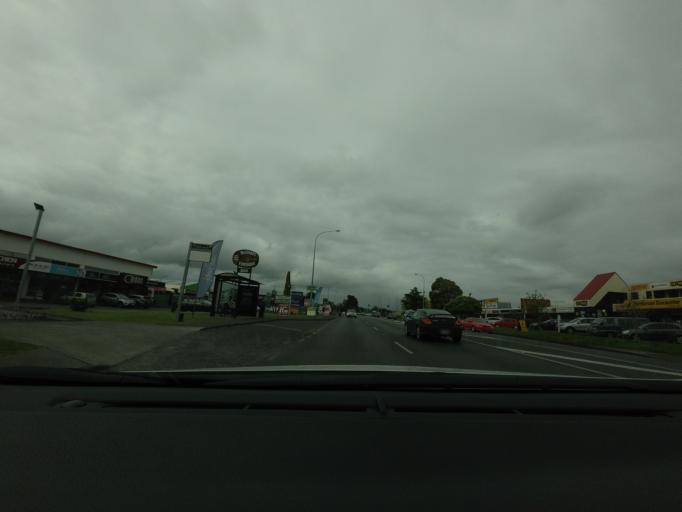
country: NZ
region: Auckland
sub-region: Auckland
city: Rosebank
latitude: -36.8554
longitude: 174.6301
